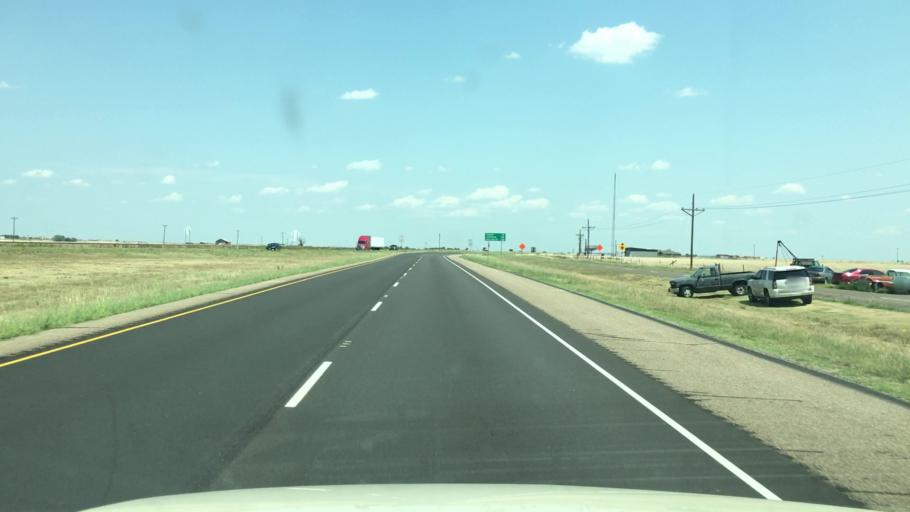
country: US
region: Texas
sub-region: Potter County
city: Amarillo
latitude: 35.1927
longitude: -101.6883
